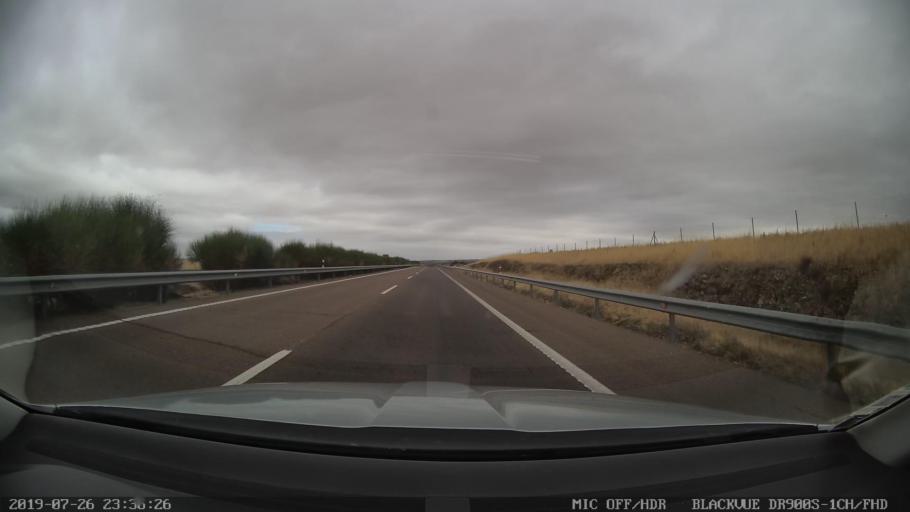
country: ES
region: Extremadura
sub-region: Provincia de Caceres
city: Trujillo
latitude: 39.3939
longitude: -5.8876
